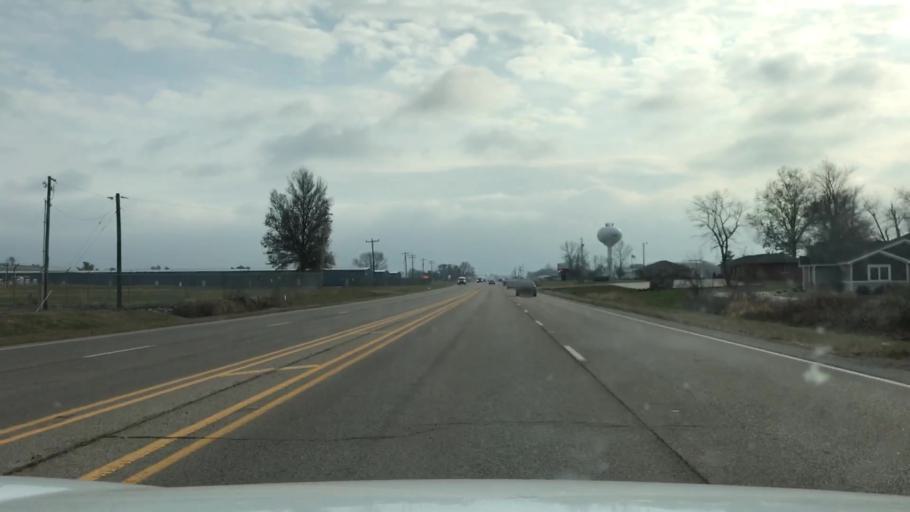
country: US
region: Illinois
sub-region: Madison County
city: Bethalto
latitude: 38.8953
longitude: -90.0594
